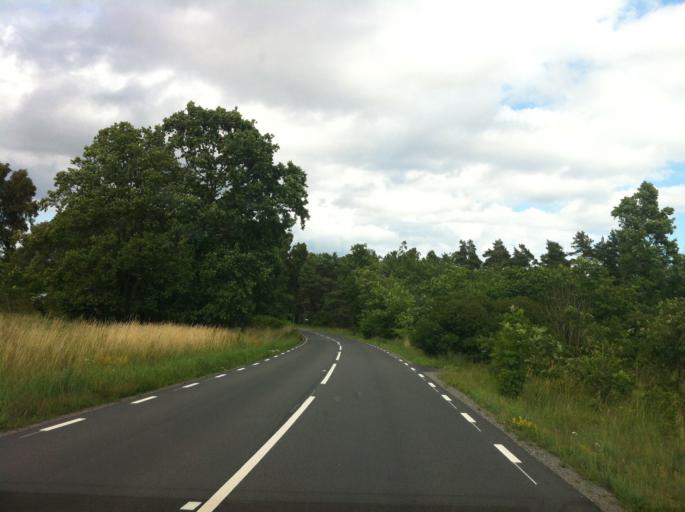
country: SE
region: Skane
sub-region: Ystads Kommun
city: Kopingebro
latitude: 55.3953
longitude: 14.1513
